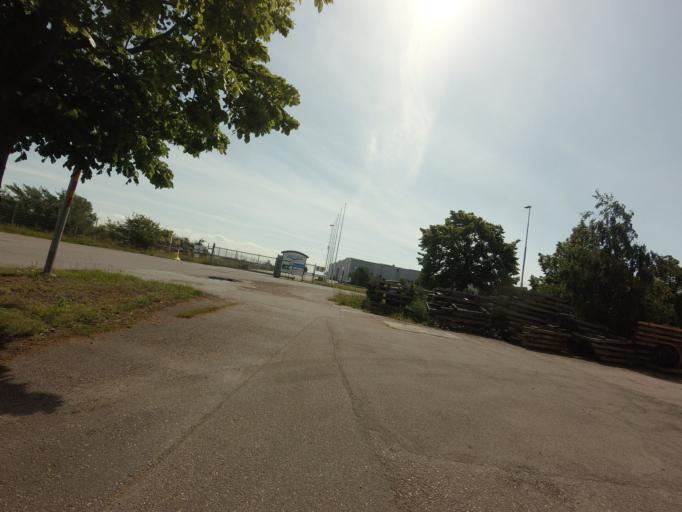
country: SE
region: Skane
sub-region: Landskrona
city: Landskrona
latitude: 55.8578
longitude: 12.8427
